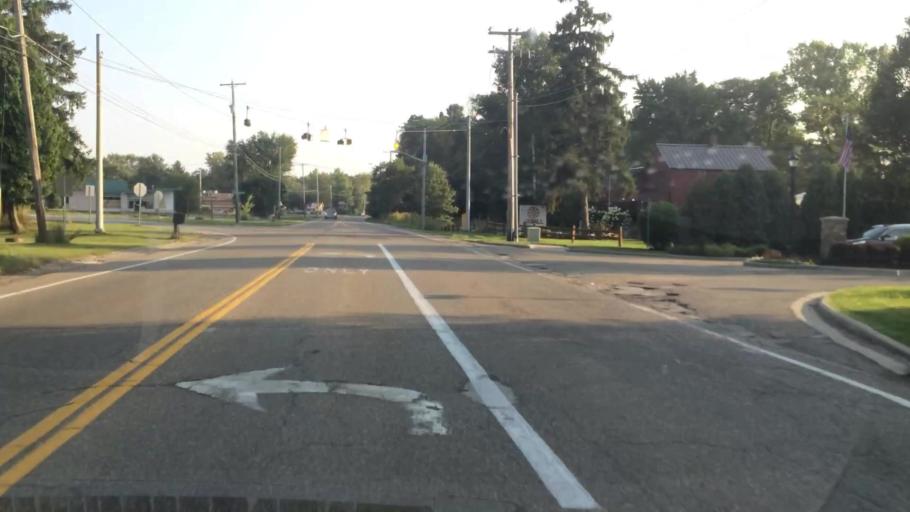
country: US
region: Ohio
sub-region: Summit County
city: Silver Lake
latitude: 41.2053
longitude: -81.4952
